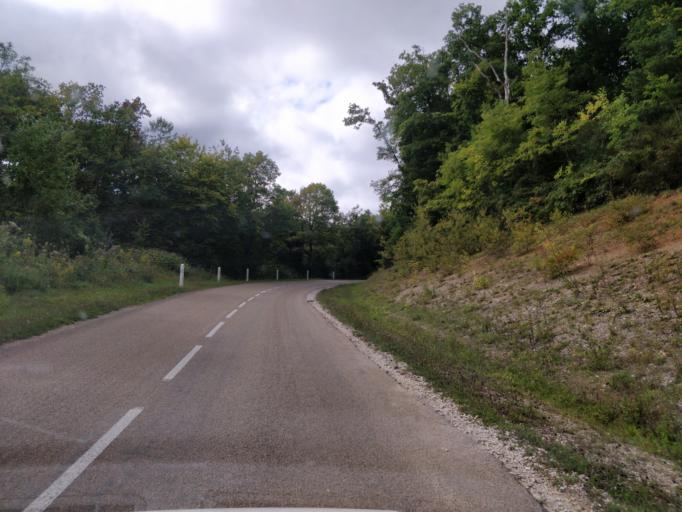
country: FR
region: Bourgogne
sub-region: Departement de l'Yonne
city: Saint-Florentin
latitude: 48.0974
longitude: 3.6836
